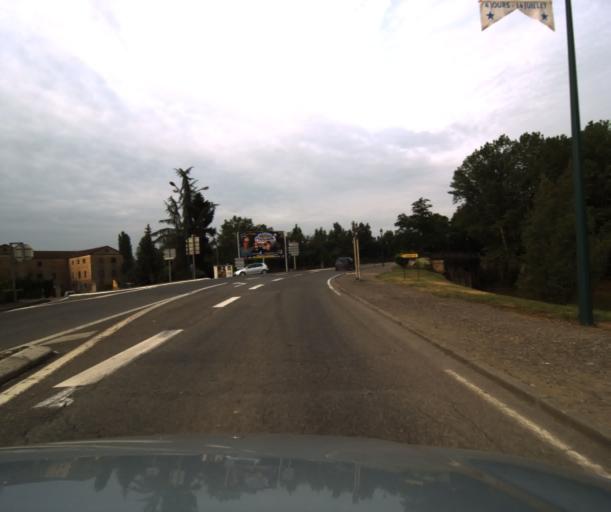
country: FR
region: Midi-Pyrenees
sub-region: Departement du Gers
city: Mirande
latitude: 43.5162
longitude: 0.4126
